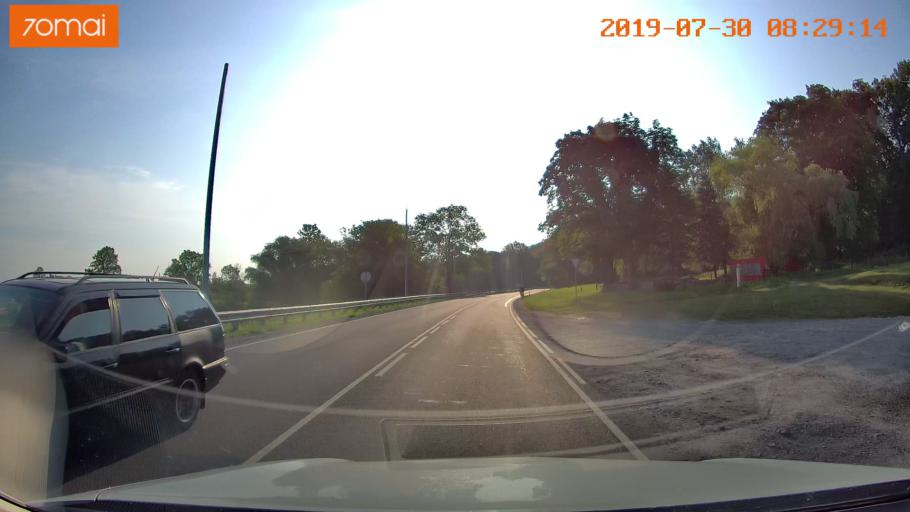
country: RU
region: Kaliningrad
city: Chernyakhovsk
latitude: 54.6312
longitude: 21.6588
